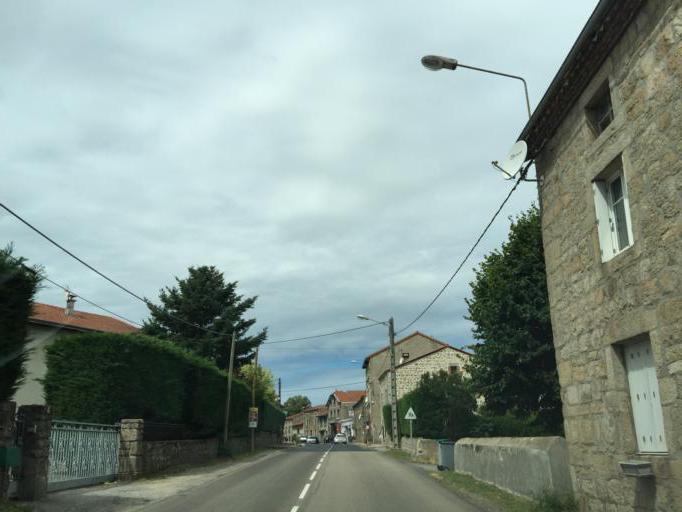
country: FR
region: Rhone-Alpes
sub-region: Departement de la Loire
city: Saint-Maurice-en-Gourgois
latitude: 45.4034
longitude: 4.1849
